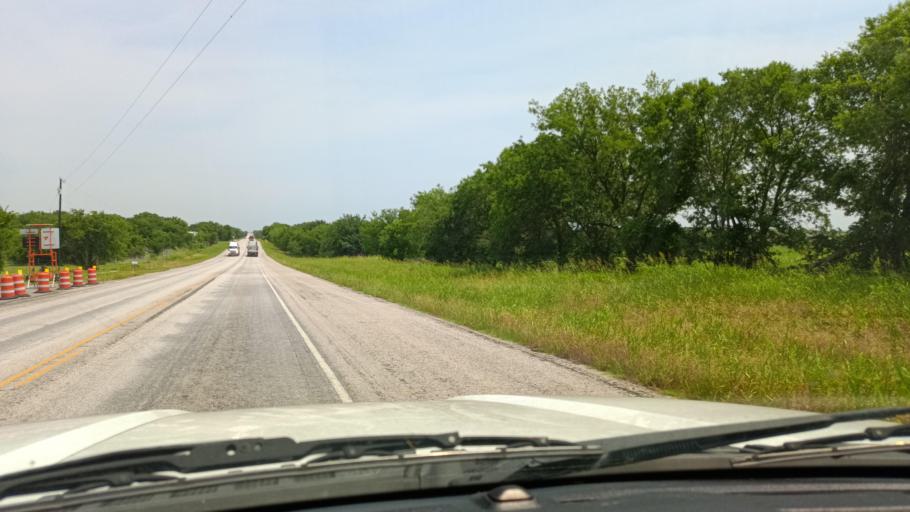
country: US
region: Texas
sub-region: Bell County
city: Rogers
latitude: 30.9463
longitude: -97.2468
